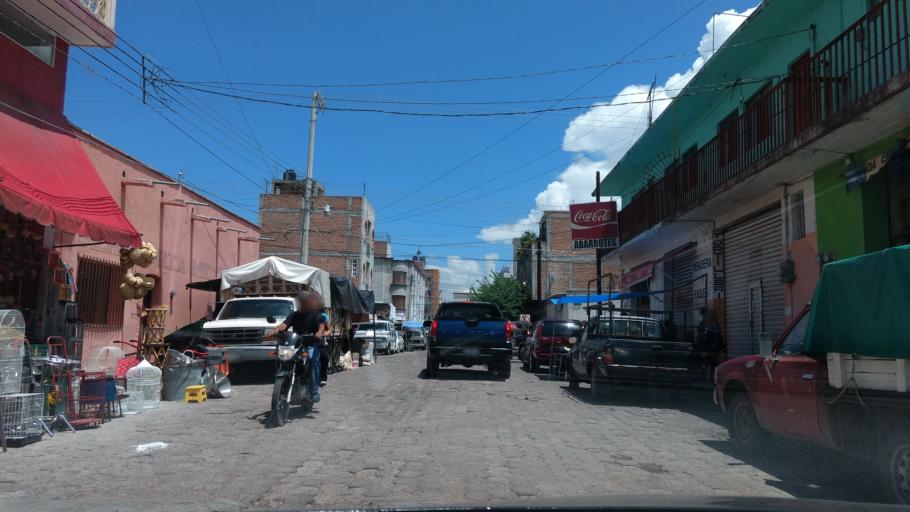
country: MX
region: Zacatecas
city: Tlaltenango de Sanchez Roman
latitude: 21.7808
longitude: -103.3039
